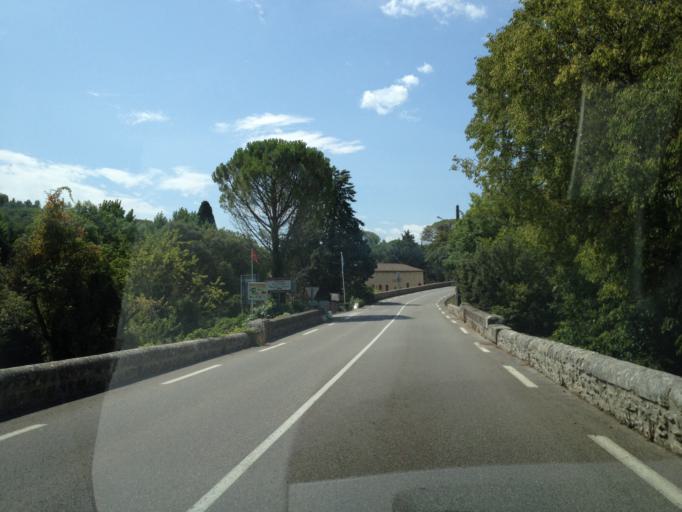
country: FR
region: Languedoc-Roussillon
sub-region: Departement du Gard
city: Saint-Mamert-du-Gard
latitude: 43.8795
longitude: 4.0963
